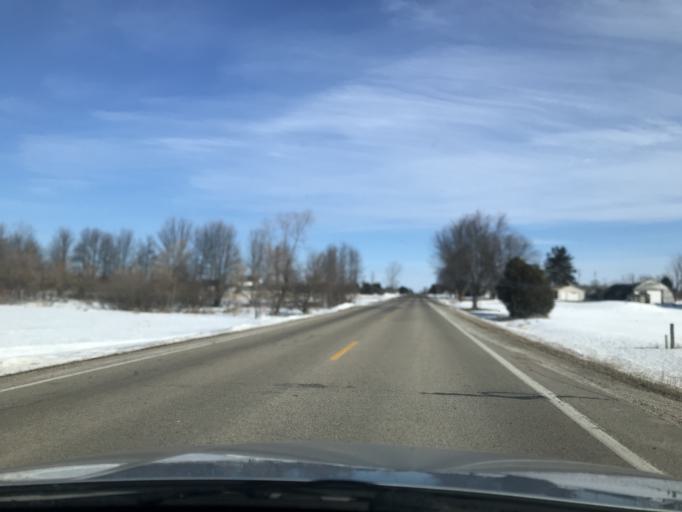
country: US
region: Wisconsin
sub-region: Oconto County
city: Oconto Falls
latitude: 44.8953
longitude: -88.1560
